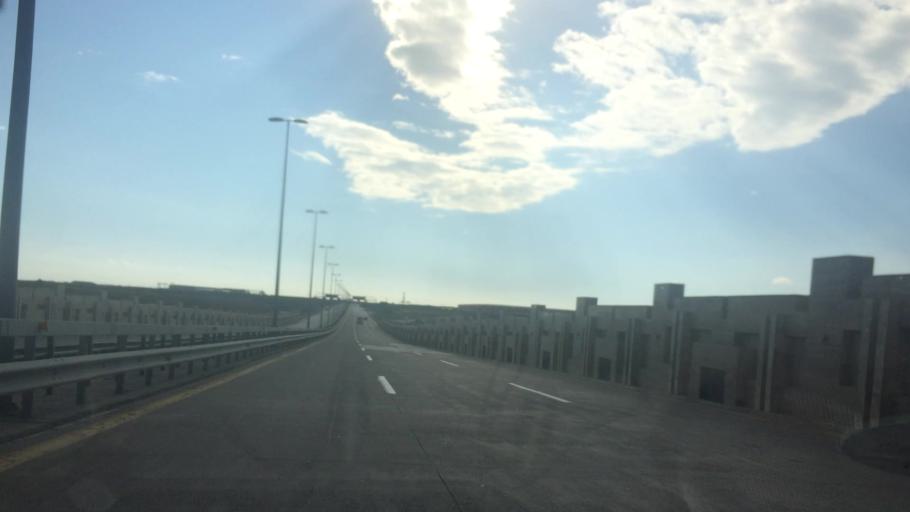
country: AZ
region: Baki
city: Hovsan
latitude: 40.3902
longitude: 50.0711
